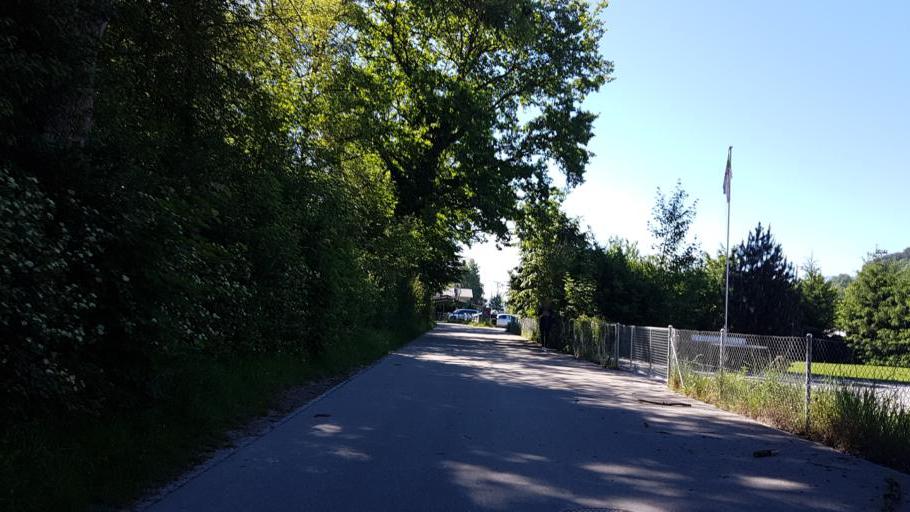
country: CH
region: Bern
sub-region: Bern-Mittelland District
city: Munsingen
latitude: 46.8659
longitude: 7.5513
